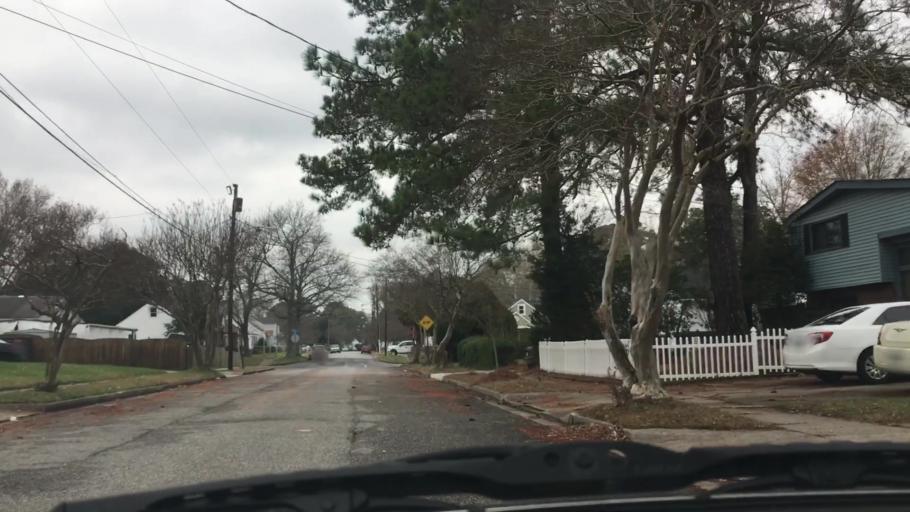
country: US
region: Virginia
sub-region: City of Norfolk
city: Norfolk
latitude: 36.8748
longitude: -76.2382
